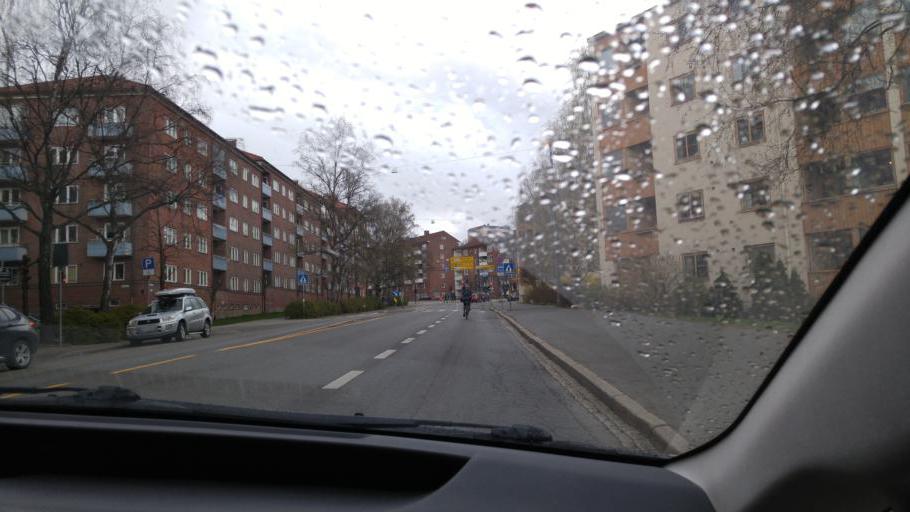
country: NO
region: Oslo
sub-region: Oslo
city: Oslo
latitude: 59.9229
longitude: 10.7735
